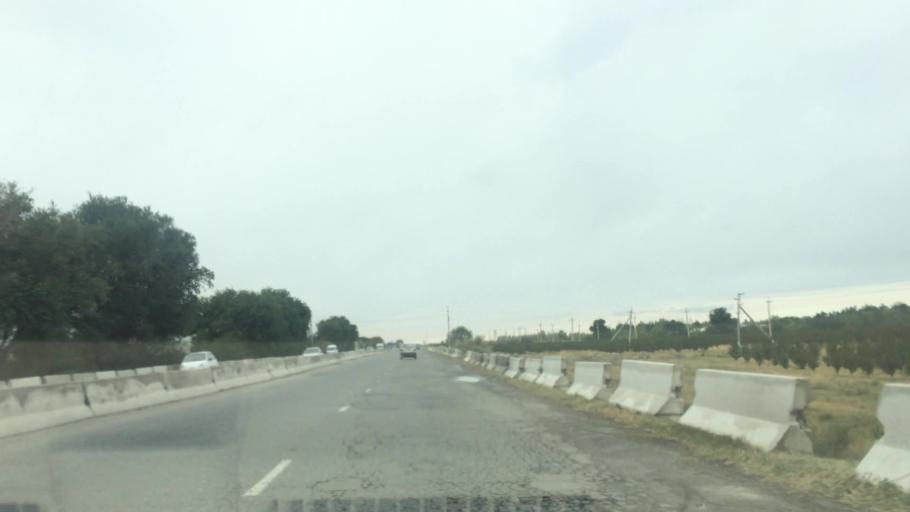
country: UZ
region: Samarqand
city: Bulung'ur
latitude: 39.7522
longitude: 67.2281
